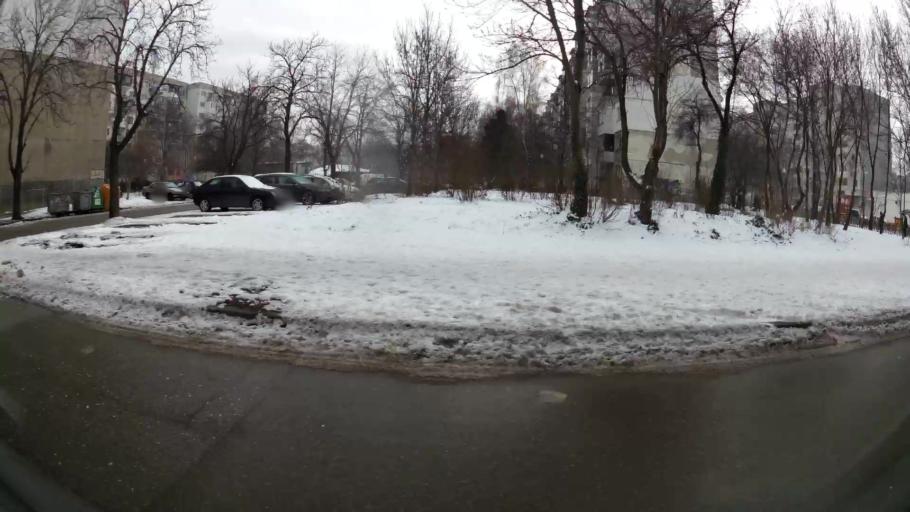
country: BG
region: Sofia-Capital
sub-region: Stolichna Obshtina
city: Sofia
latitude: 42.7116
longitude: 23.2932
